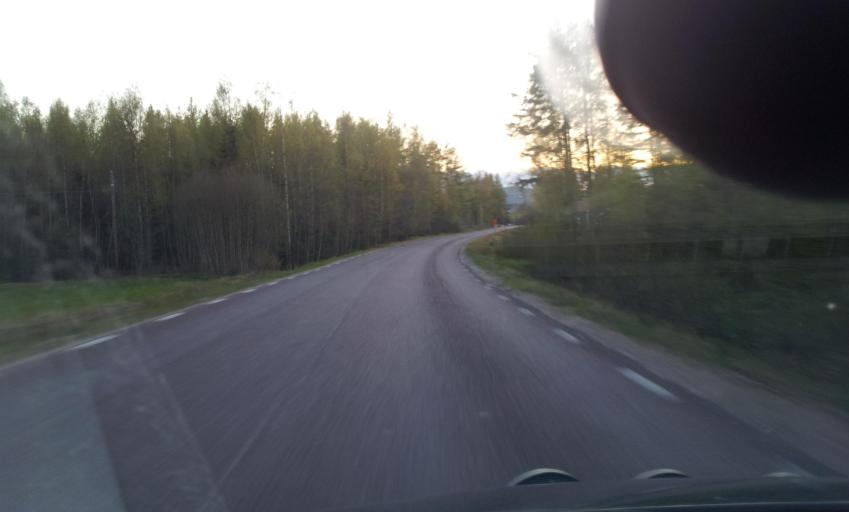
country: SE
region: Gaevleborg
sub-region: Bollnas Kommun
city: Bollnas
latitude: 61.3889
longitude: 16.4239
